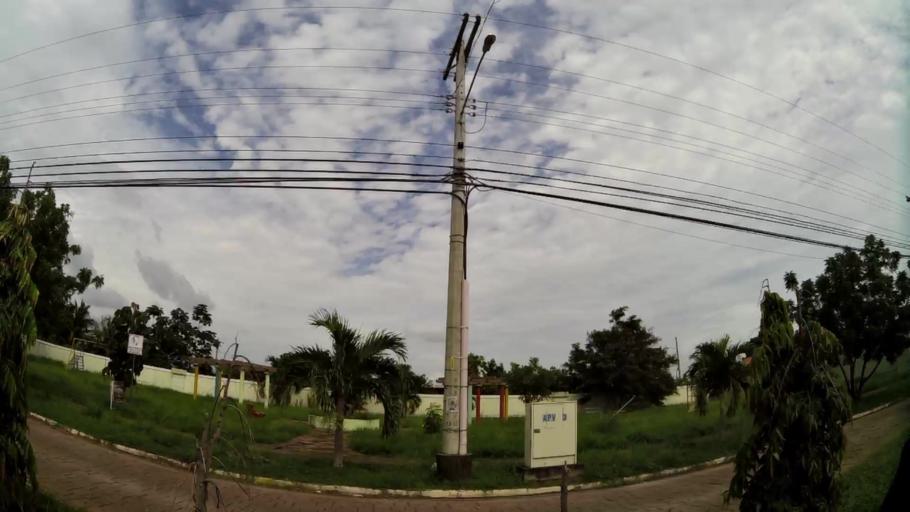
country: PA
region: Panama
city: Tocumen
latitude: 9.0440
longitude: -79.4124
